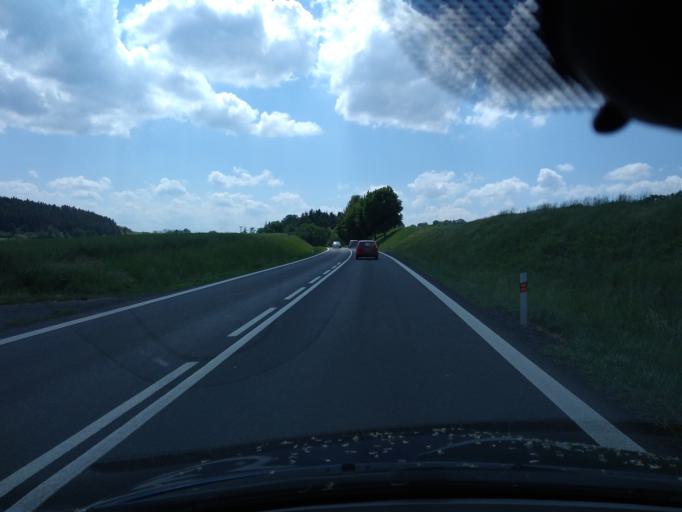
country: CZ
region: Plzensky
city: Svihov
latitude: 49.4413
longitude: 13.2851
